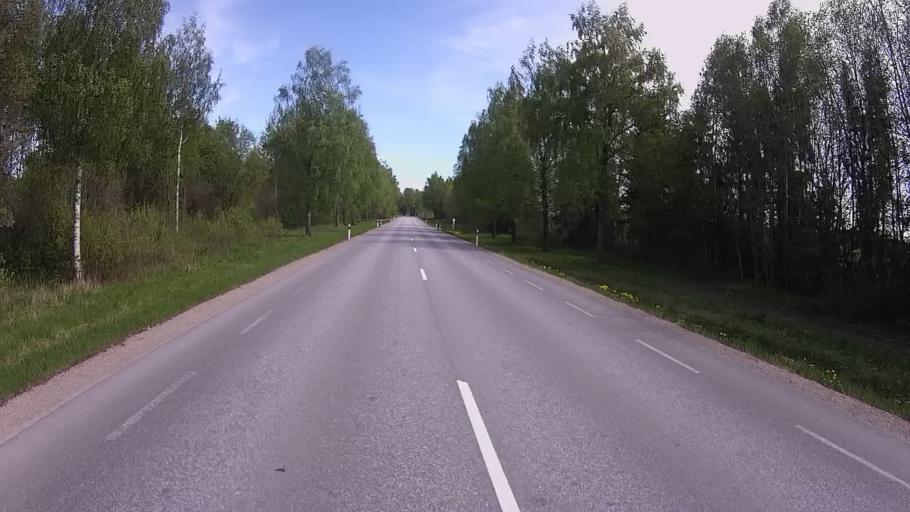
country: EE
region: Valgamaa
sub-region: Valga linn
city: Valga
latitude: 57.7301
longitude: 26.1686
